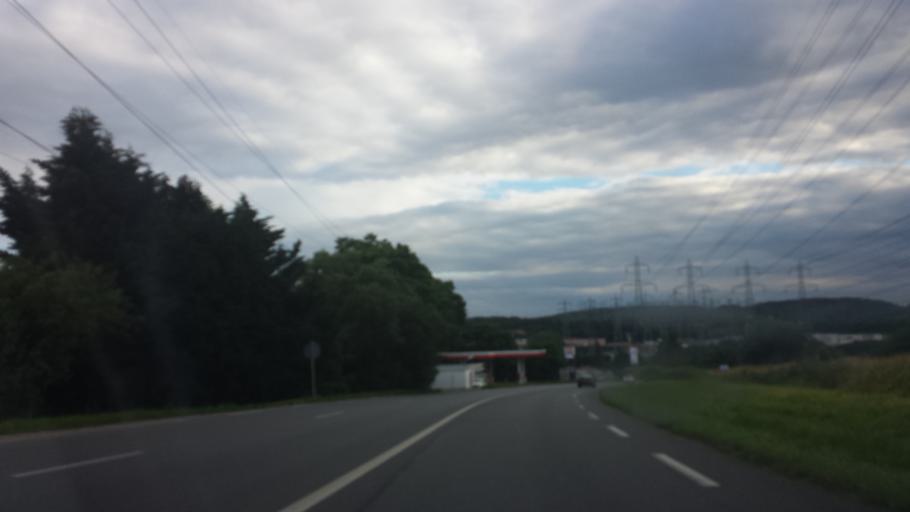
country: FR
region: Ile-de-France
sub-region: Departement de l'Essonne
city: Palaiseau
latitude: 48.7107
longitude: 2.2631
